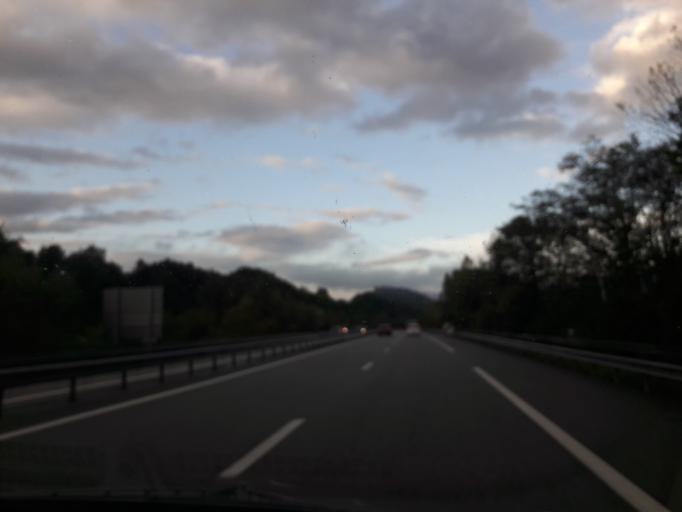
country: FR
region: Rhone-Alpes
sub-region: Departement de la Savoie
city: Aiton
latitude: 45.5611
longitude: 6.2015
